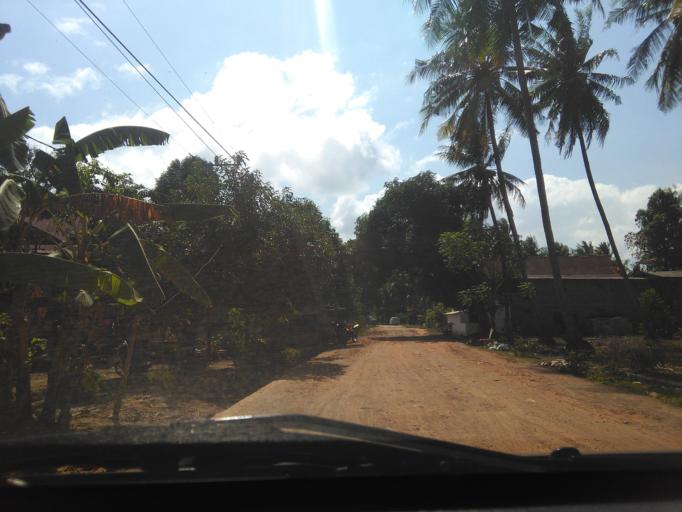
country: ID
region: South Sulawesi
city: Tancung
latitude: -4.0145
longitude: 119.9256
